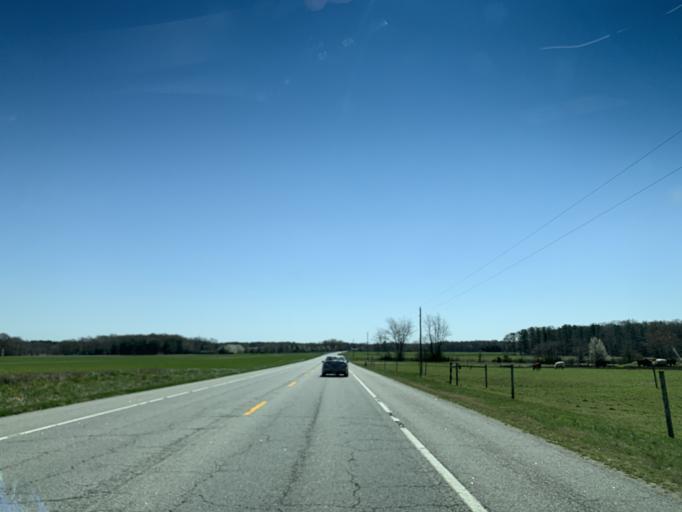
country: US
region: Maryland
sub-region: Queen Anne's County
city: Centreville
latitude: 38.9849
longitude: -76.0206
